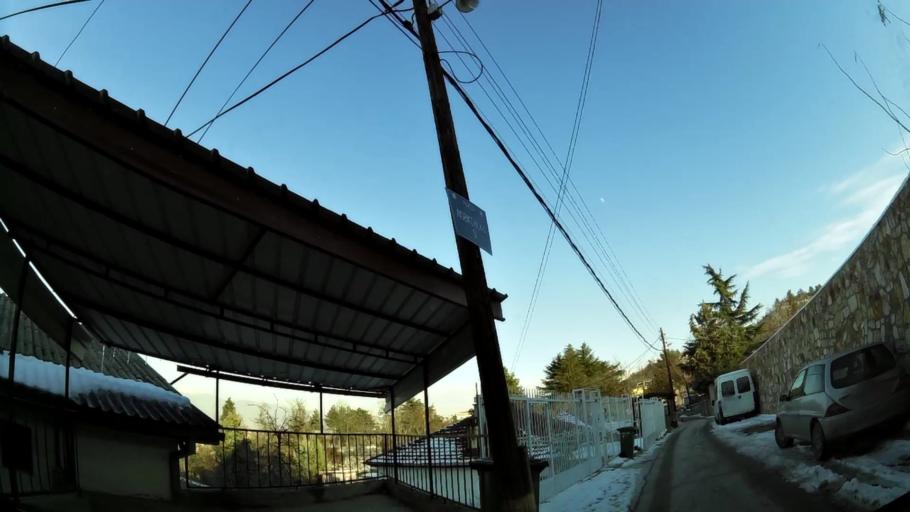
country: MK
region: Karpos
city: Skopje
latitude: 41.9901
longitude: 21.4031
